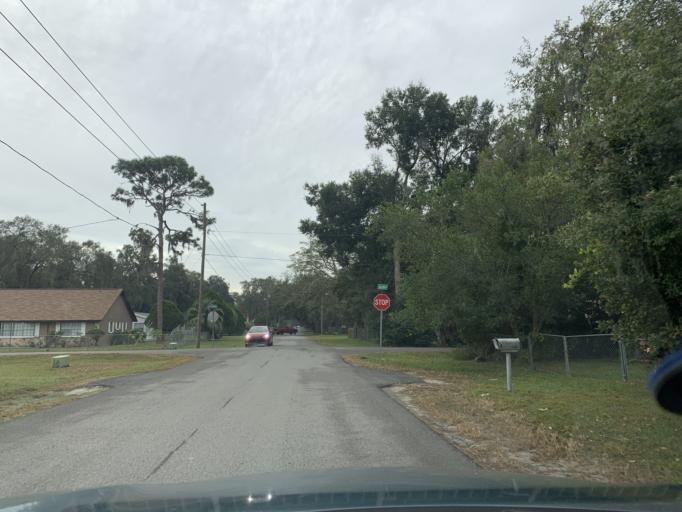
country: US
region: Florida
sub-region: Pasco County
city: Zephyrhills
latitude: 28.2256
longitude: -82.1810
